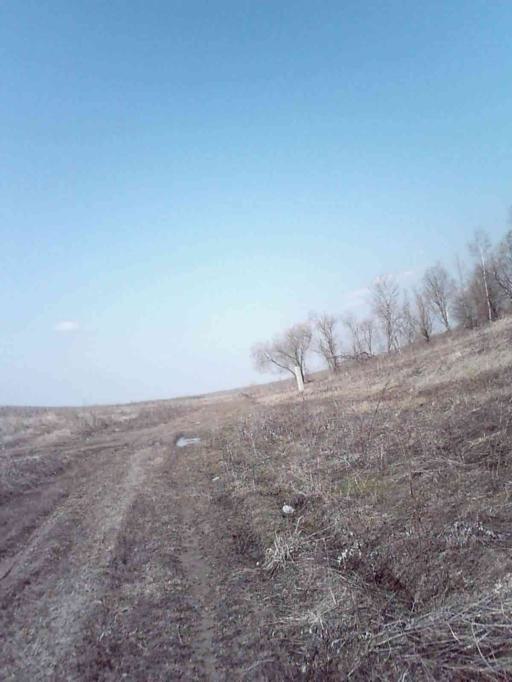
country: RU
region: Moskovskaya
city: Kommunarka
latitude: 55.5428
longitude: 37.4913
